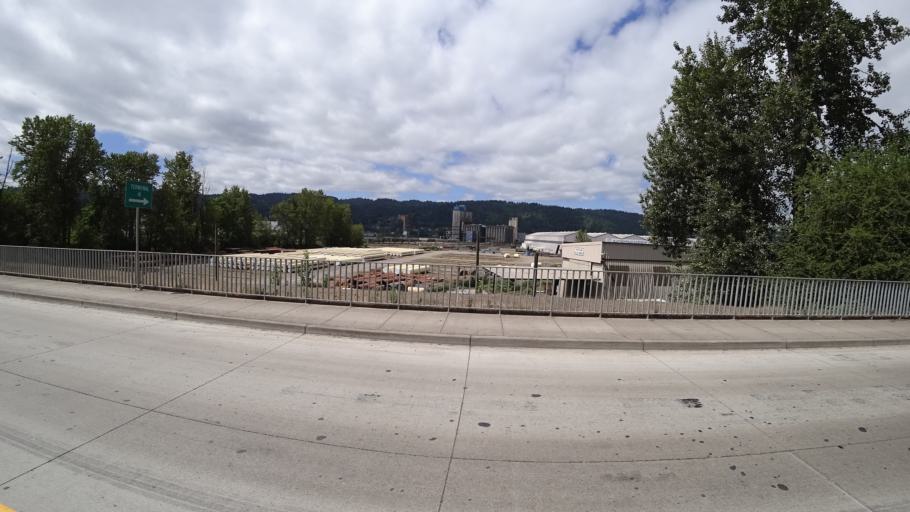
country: US
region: Oregon
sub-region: Washington County
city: West Haven
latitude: 45.6081
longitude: -122.7673
